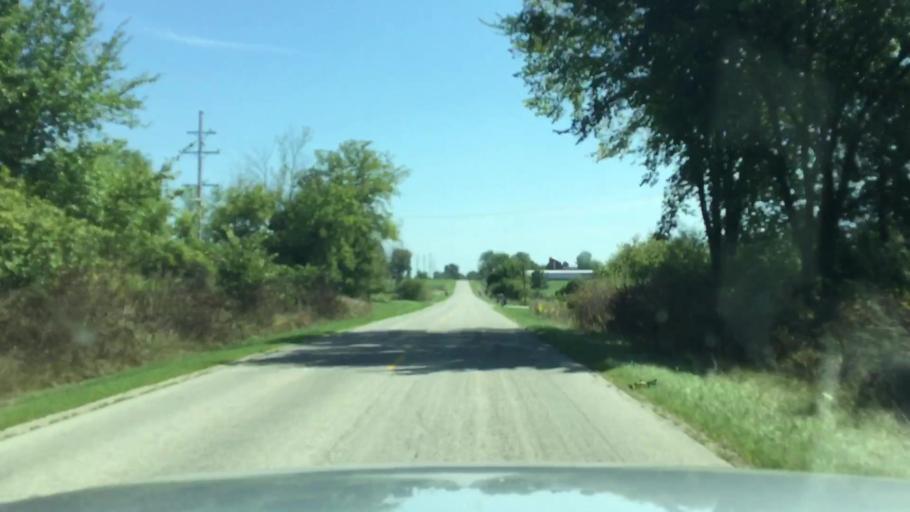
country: US
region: Michigan
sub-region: Lenawee County
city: Clinton
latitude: 42.0653
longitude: -83.9494
